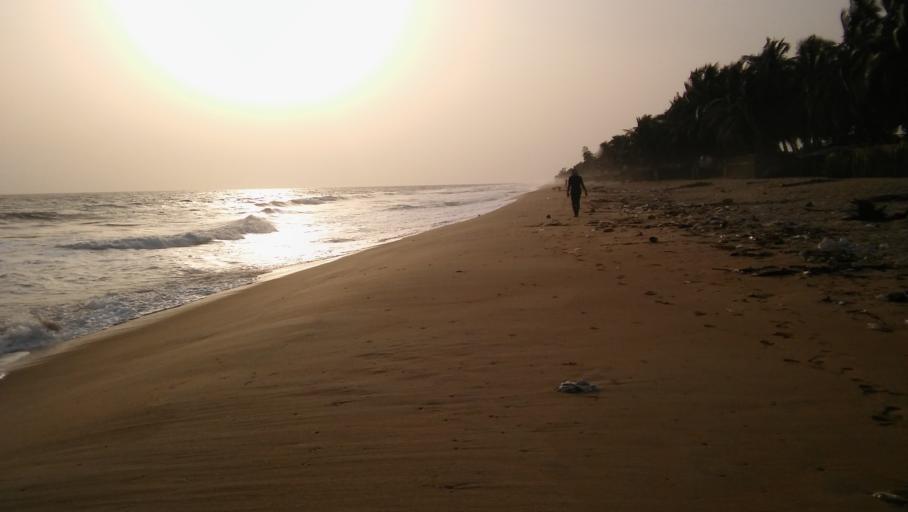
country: CI
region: Sud-Comoe
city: Grand-Bassam
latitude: 5.1922
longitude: -3.7266
